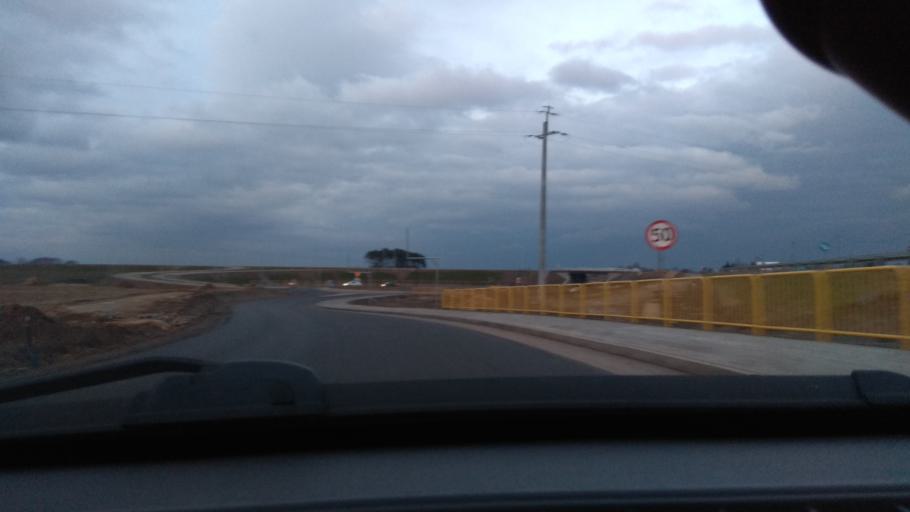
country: PL
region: Greater Poland Voivodeship
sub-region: Powiat kepinski
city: Baranow
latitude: 51.2887
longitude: 18.0189
